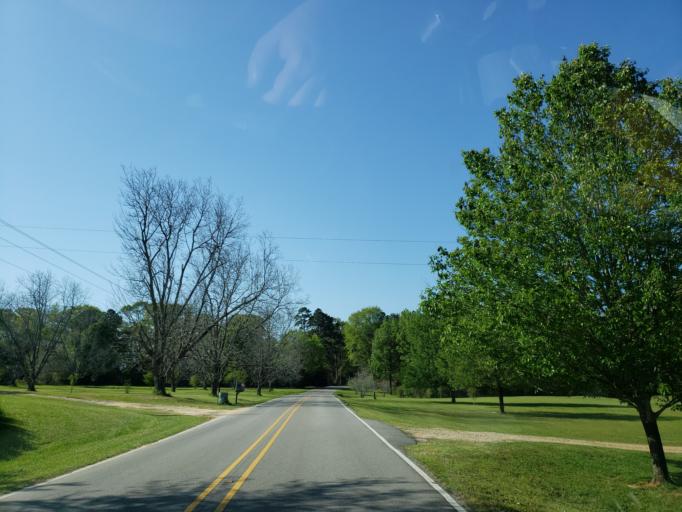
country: US
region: Mississippi
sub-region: Covington County
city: Collins
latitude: 31.6077
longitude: -89.3812
